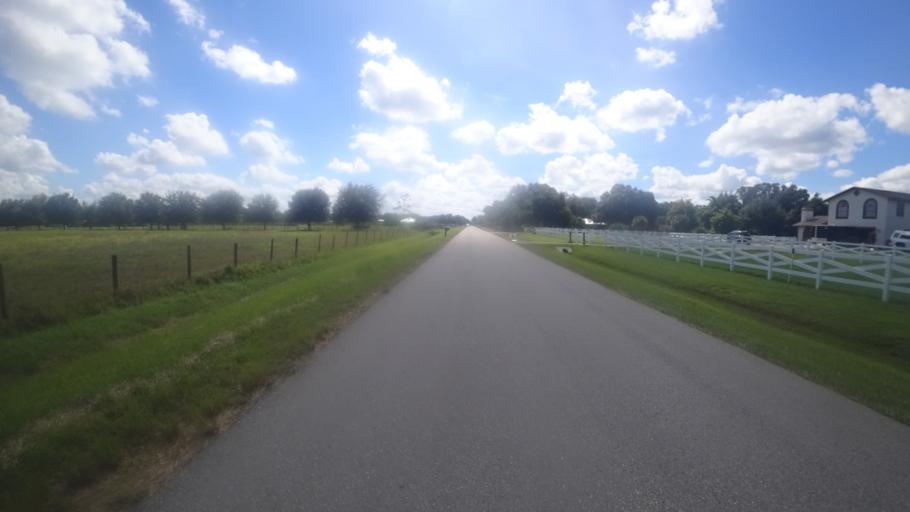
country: US
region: Florida
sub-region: Manatee County
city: Ellenton
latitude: 27.5118
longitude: -82.4295
